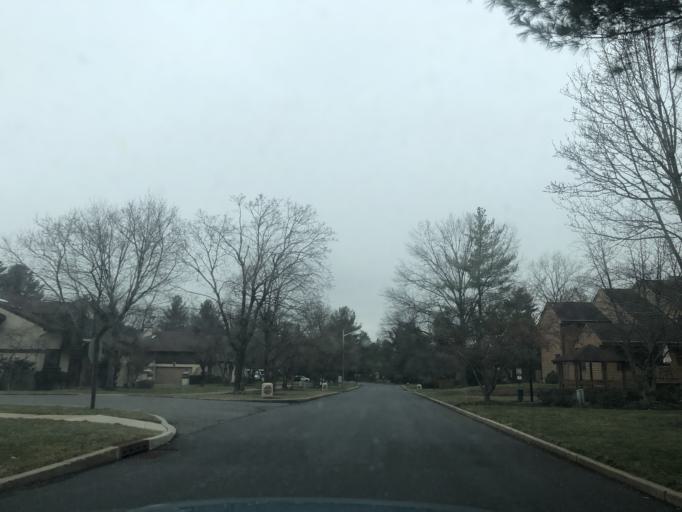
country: US
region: New Jersey
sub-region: Somerset County
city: Kingston
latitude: 40.3515
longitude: -74.6193
